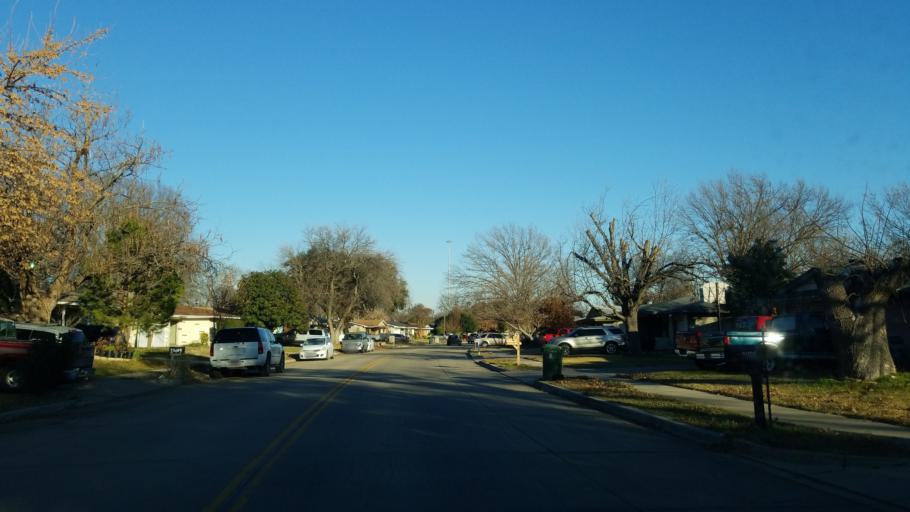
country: US
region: Texas
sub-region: Tarrant County
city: Arlington
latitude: 32.7257
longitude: -97.0667
